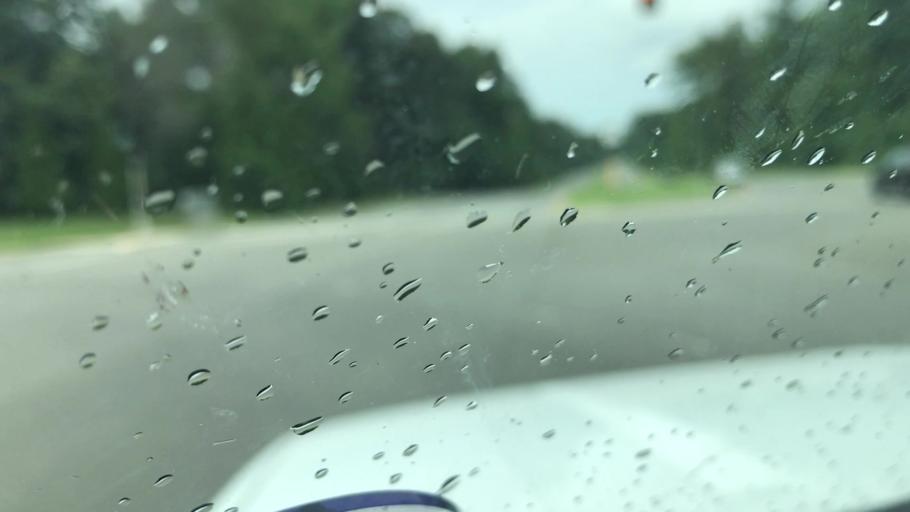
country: US
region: Virginia
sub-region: Henrico County
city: Short Pump
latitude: 37.6355
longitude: -77.6132
